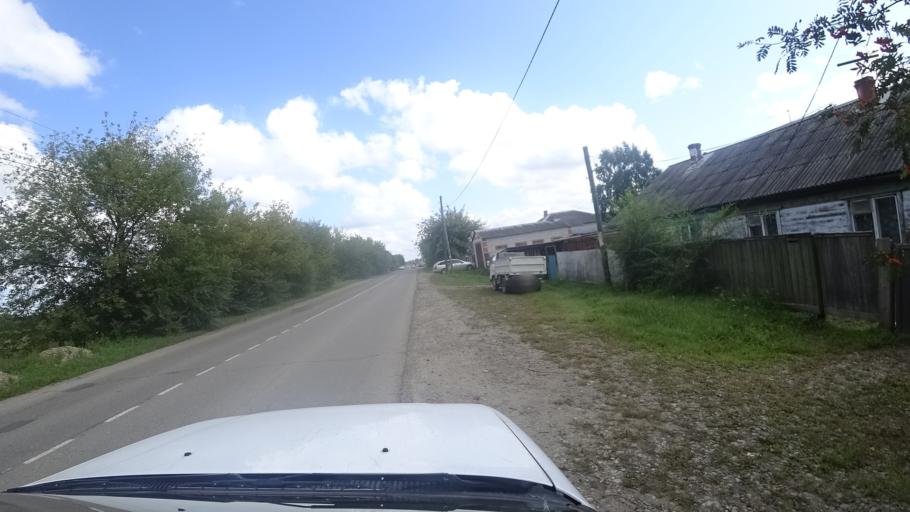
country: RU
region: Primorskiy
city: Dal'nerechensk
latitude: 45.9259
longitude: 133.7696
